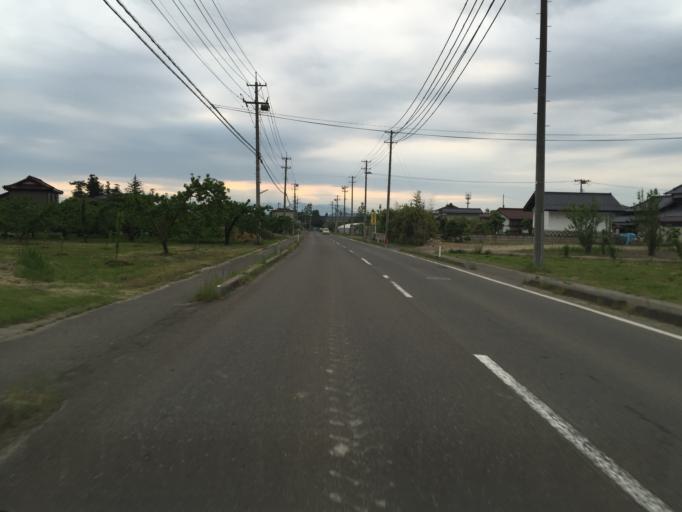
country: JP
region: Fukushima
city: Fukushima-shi
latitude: 37.8130
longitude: 140.4660
